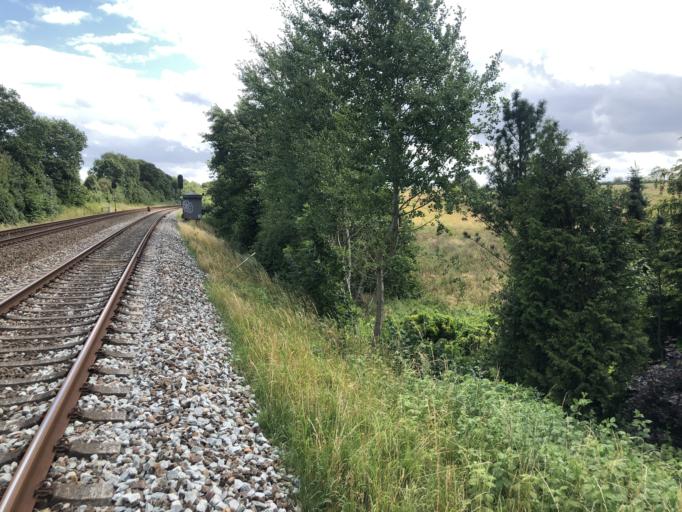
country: DK
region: South Denmark
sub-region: Vejle Kommune
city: Borkop
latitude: 55.5966
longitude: 9.6709
